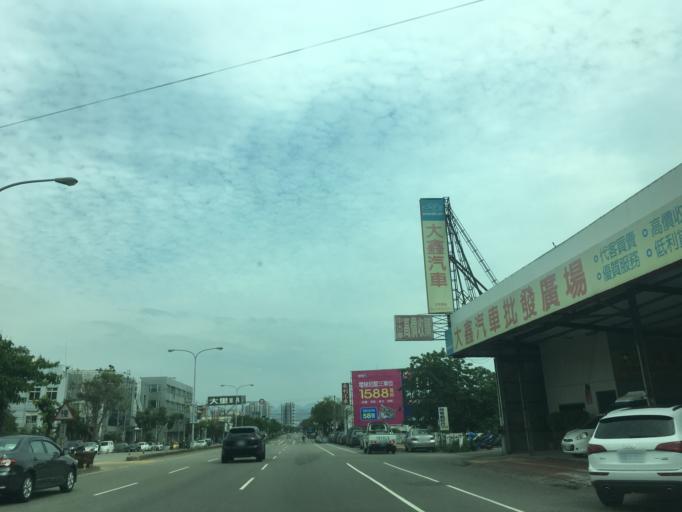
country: TW
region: Taiwan
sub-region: Taichung City
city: Taichung
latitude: 24.1083
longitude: 120.6626
